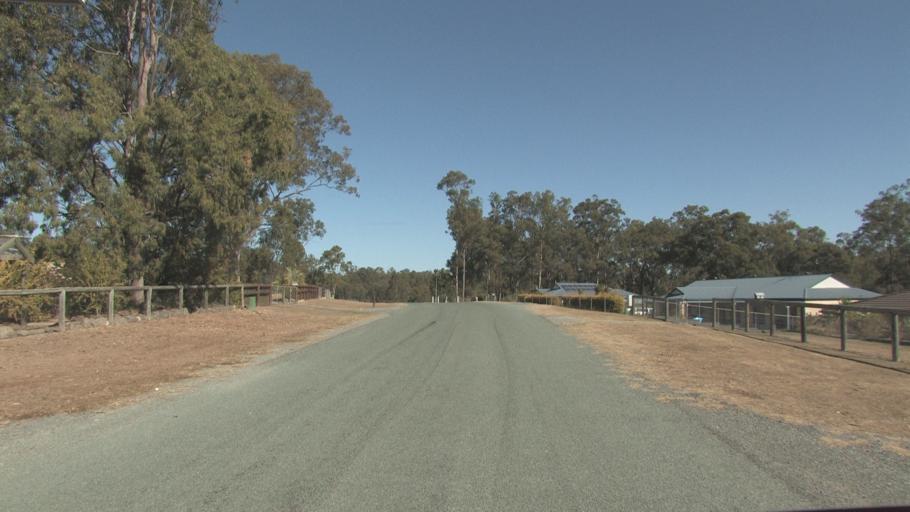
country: AU
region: Queensland
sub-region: Logan
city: Cedar Vale
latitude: -27.8640
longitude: 153.0334
